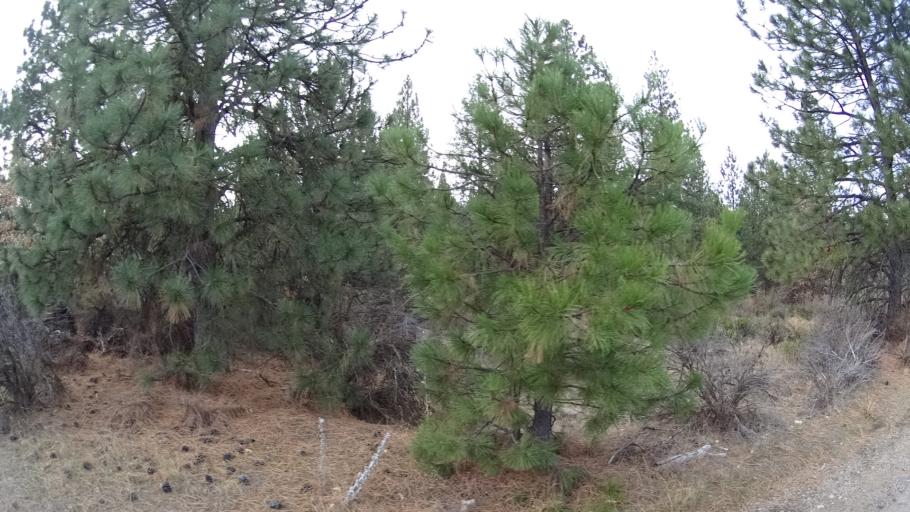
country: US
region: California
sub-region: Siskiyou County
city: Weed
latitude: 41.4425
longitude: -122.3720
